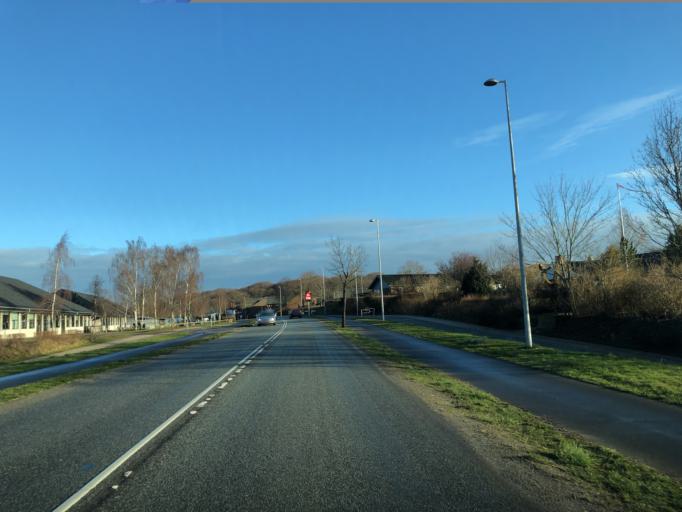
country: DK
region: Central Jutland
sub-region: Favrskov Kommune
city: Hinnerup
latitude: 56.2582
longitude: 10.0706
